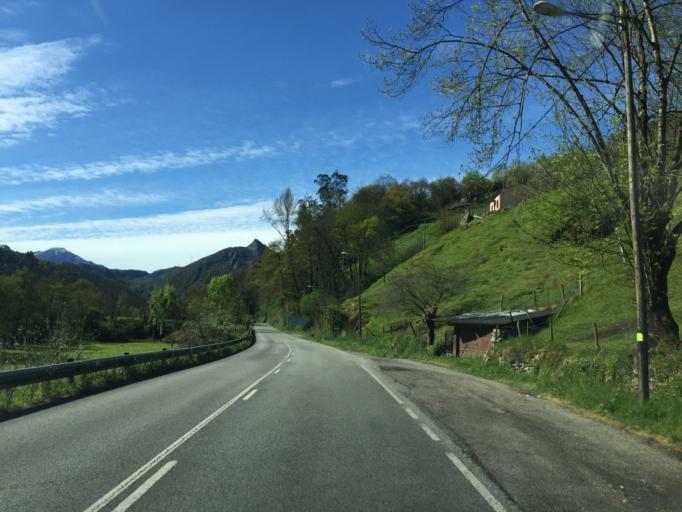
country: ES
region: Asturias
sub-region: Province of Asturias
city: Proaza
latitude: 43.3351
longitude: -5.9867
